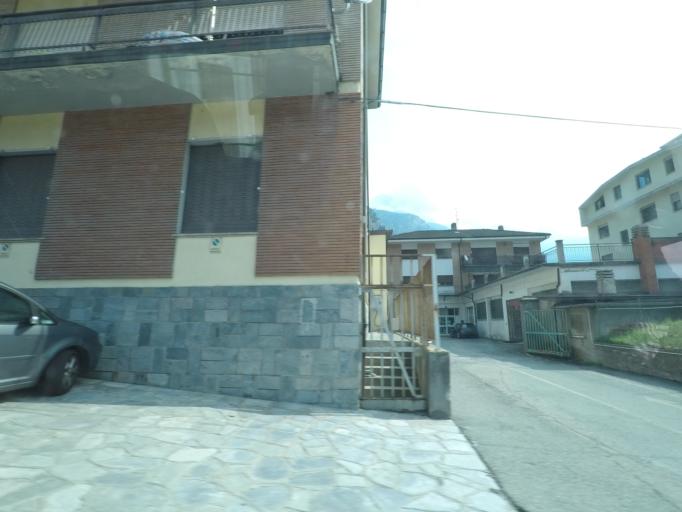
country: IT
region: Aosta Valley
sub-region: Valle d'Aosta
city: Chatillon
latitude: 45.7505
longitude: 7.6149
